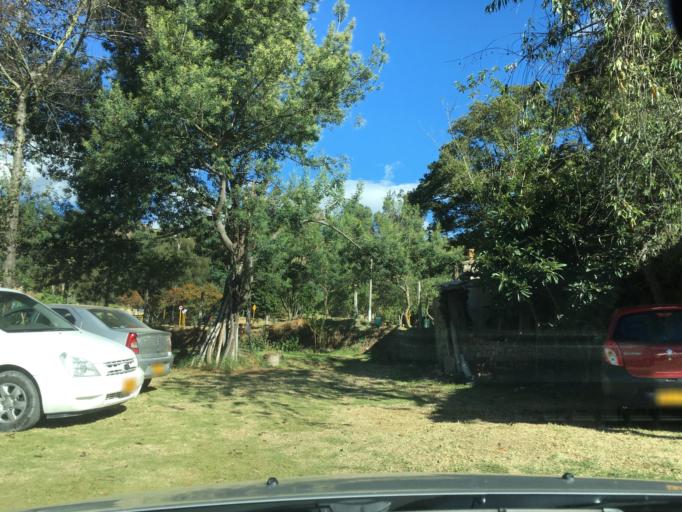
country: CO
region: Boyaca
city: Sogamoso
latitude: 5.7100
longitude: -72.9239
